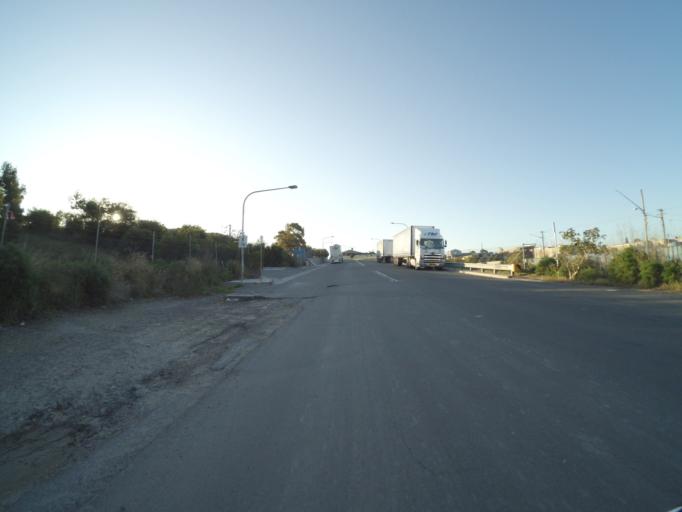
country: AU
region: New South Wales
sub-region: Botany Bay
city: Mascot
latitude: -33.9221
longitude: 151.1695
